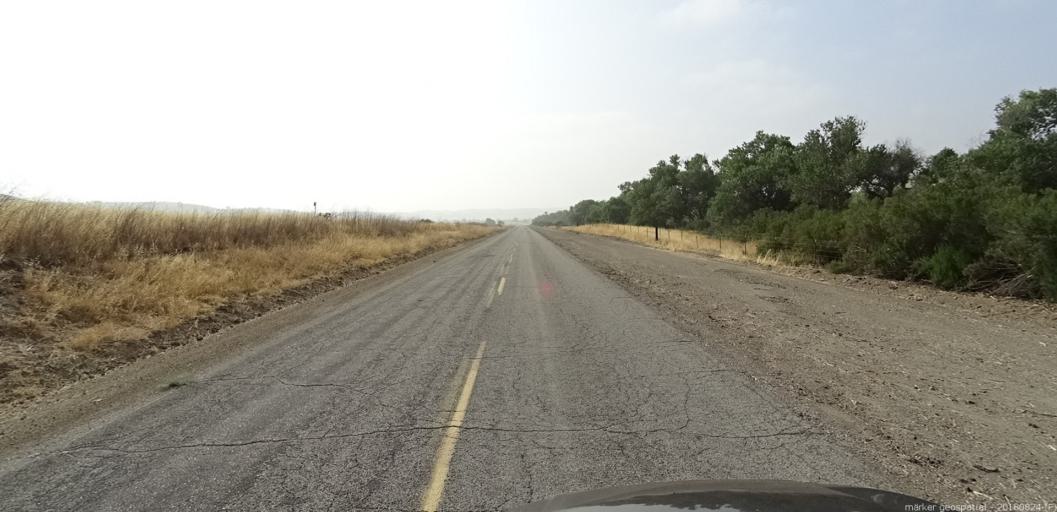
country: US
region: California
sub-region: San Luis Obispo County
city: San Miguel
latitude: 35.8577
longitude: -120.7636
